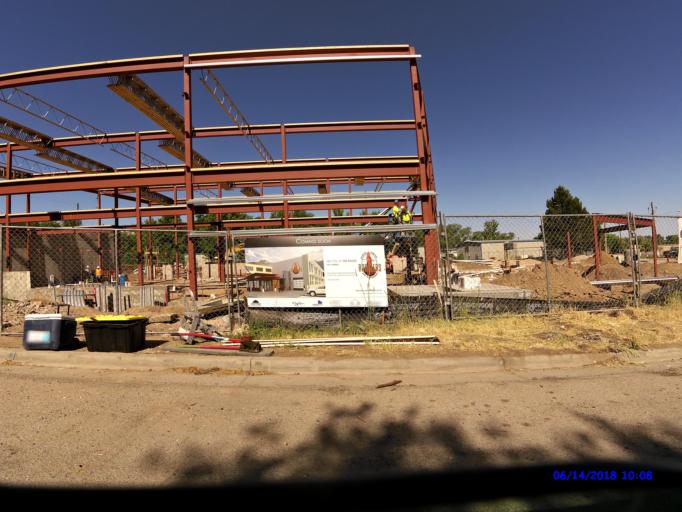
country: US
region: Utah
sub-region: Weber County
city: Ogden
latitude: 41.2246
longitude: -111.9910
